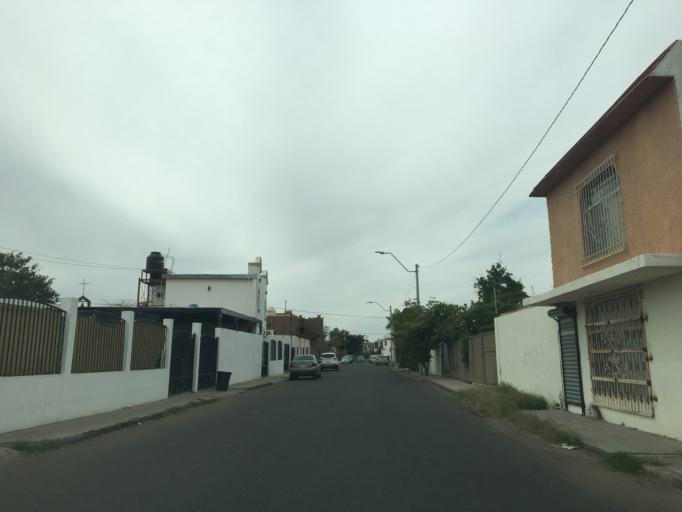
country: MX
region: Sonora
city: Hermosillo
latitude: 29.0763
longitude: -110.9697
